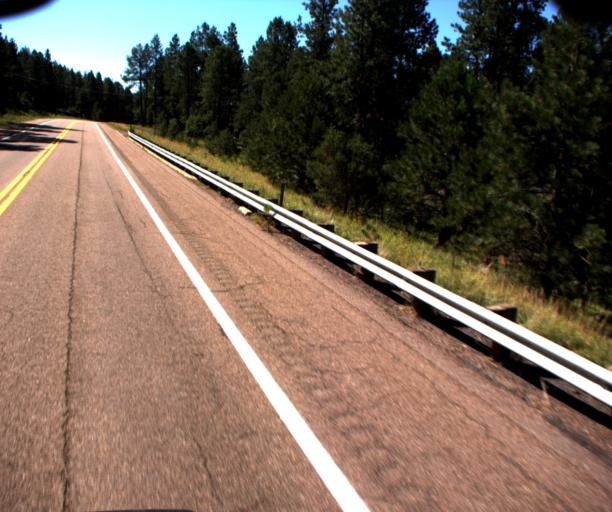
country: US
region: Arizona
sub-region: Apache County
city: Eagar
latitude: 33.8645
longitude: -109.1636
